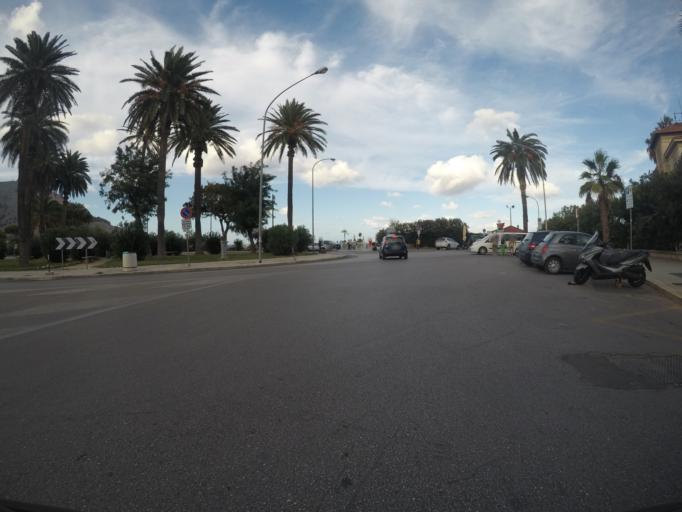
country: IT
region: Sicily
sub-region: Palermo
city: Palermo
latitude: 38.1966
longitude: 13.3319
